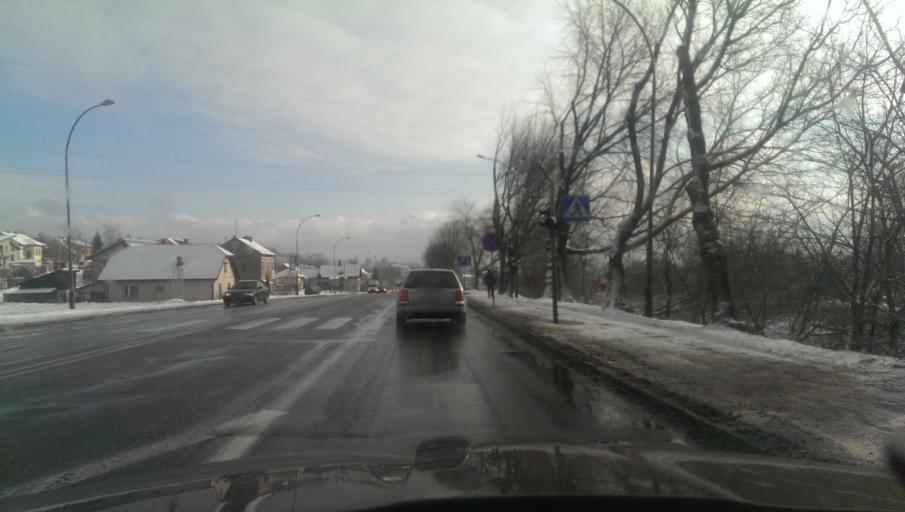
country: PL
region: Subcarpathian Voivodeship
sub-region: Powiat sanocki
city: Sanok
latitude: 49.5641
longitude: 22.1814
